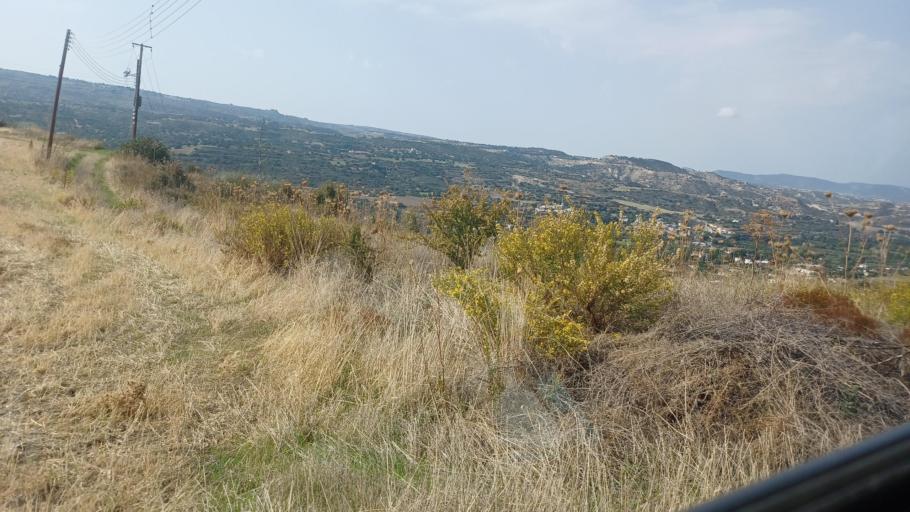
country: CY
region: Pafos
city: Polis
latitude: 34.9879
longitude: 32.4585
